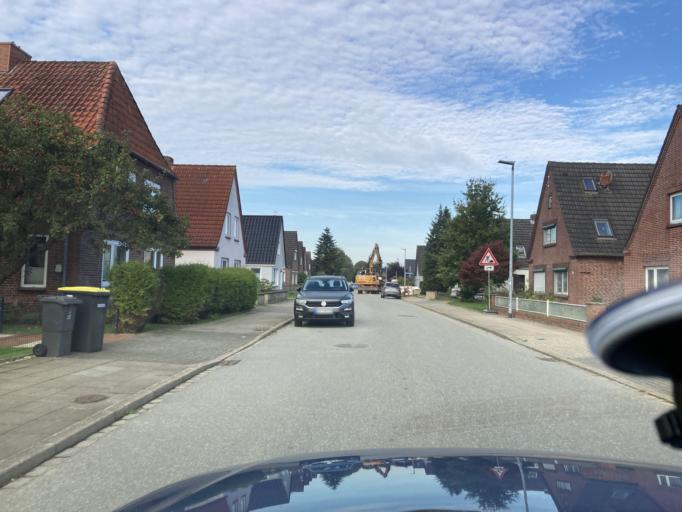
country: DE
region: Schleswig-Holstein
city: Wesseln
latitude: 54.1961
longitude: 9.0796
